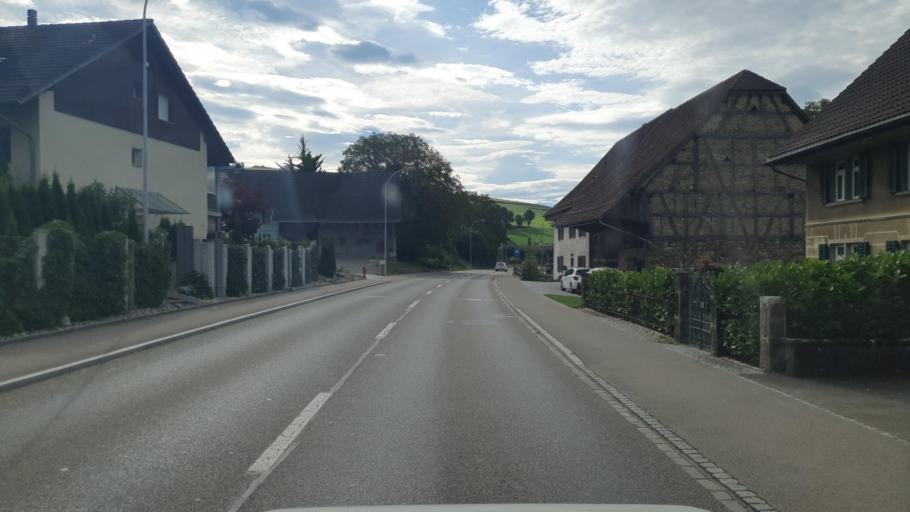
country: CH
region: Aargau
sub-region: Bezirk Bremgarten
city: Sarmenstorf
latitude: 47.3074
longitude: 8.2481
